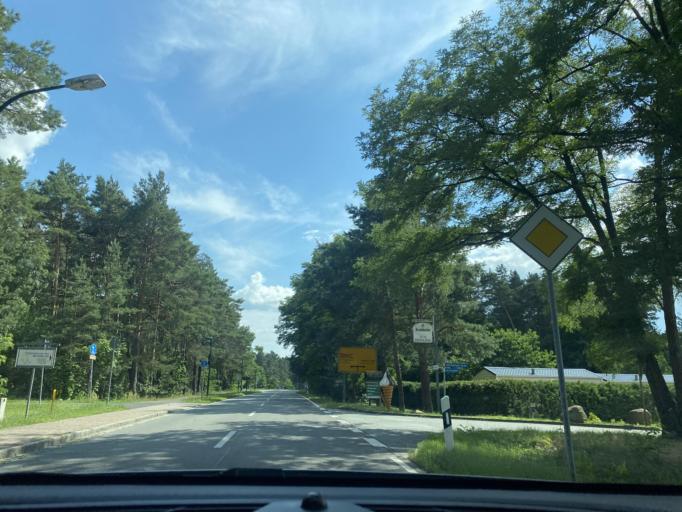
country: DE
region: Saxony
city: Boxberg
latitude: 51.4022
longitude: 14.5742
